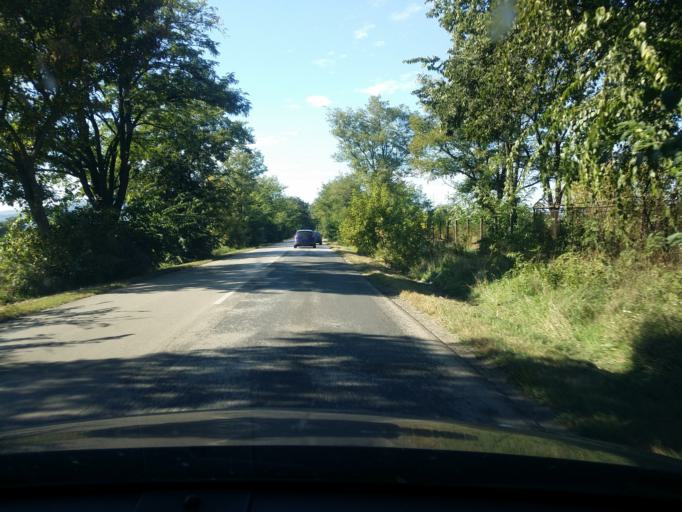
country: HU
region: Pest
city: God
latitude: 47.6859
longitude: 19.1647
